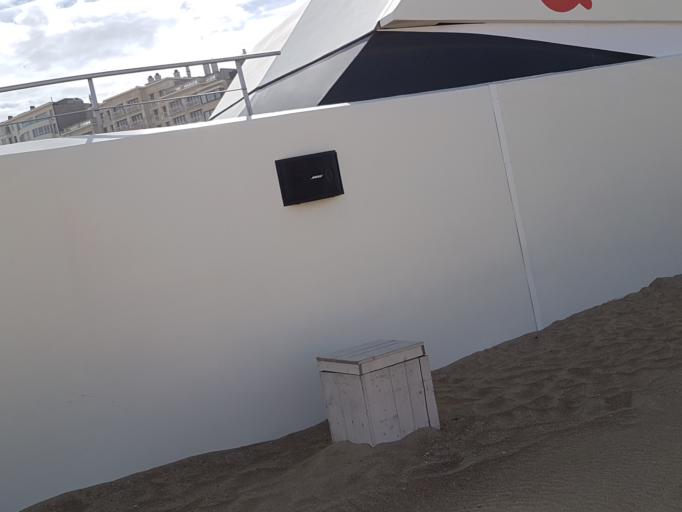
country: BE
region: Flanders
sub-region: Provincie West-Vlaanderen
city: Ostend
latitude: 51.2297
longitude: 2.9077
